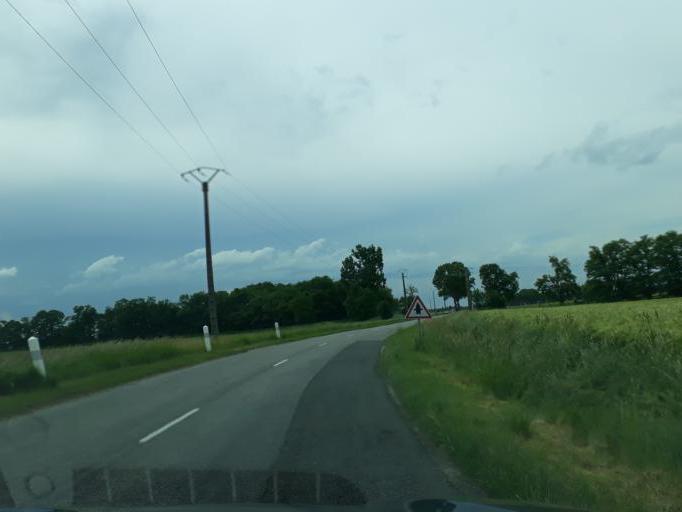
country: FR
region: Centre
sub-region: Departement du Loiret
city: Vienne-en-Val
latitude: 47.8244
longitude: 2.1512
